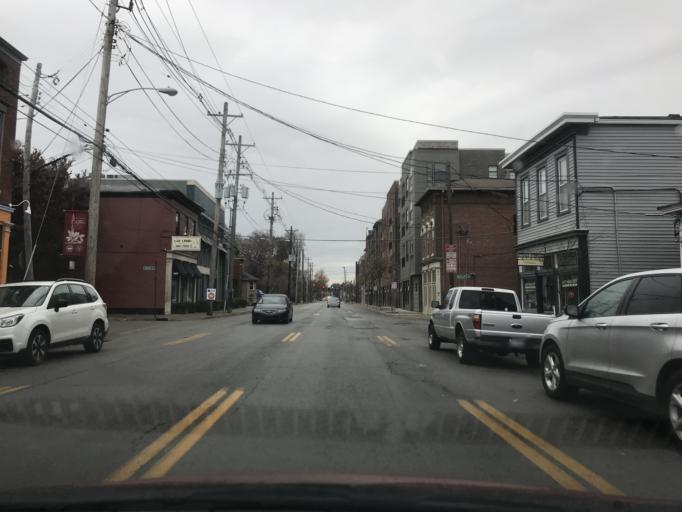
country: US
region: Kentucky
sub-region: Jefferson County
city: Louisville
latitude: 38.2457
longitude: -85.7285
